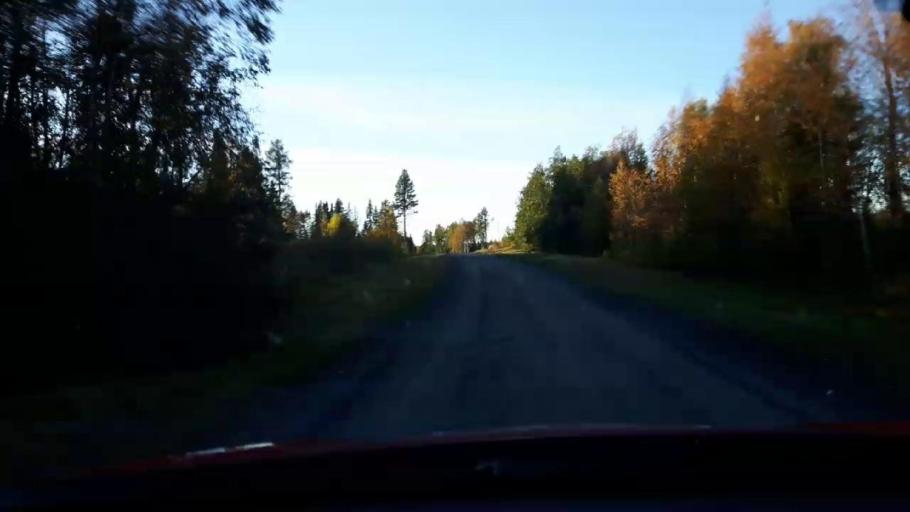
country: SE
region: Jaemtland
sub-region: Krokoms Kommun
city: Krokom
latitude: 63.4370
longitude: 14.6050
